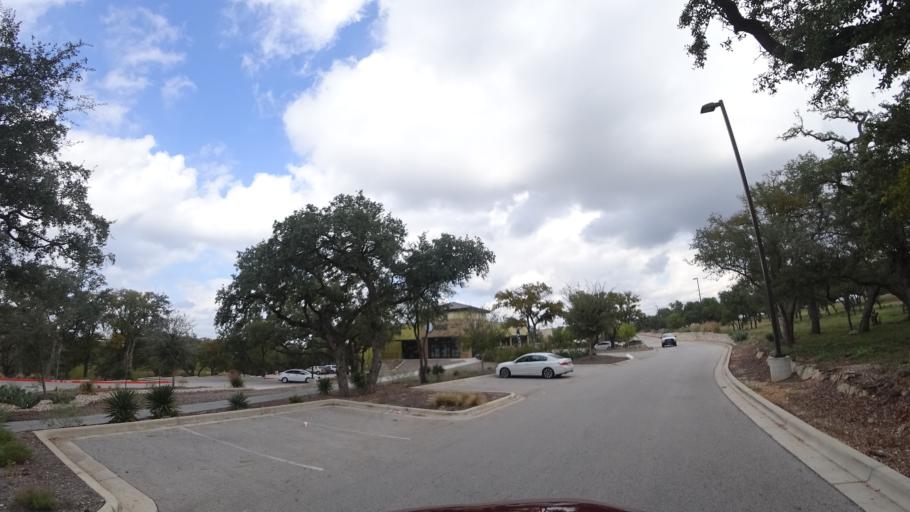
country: US
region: Texas
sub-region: Williamson County
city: Anderson Mill
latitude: 30.4193
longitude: -97.8469
